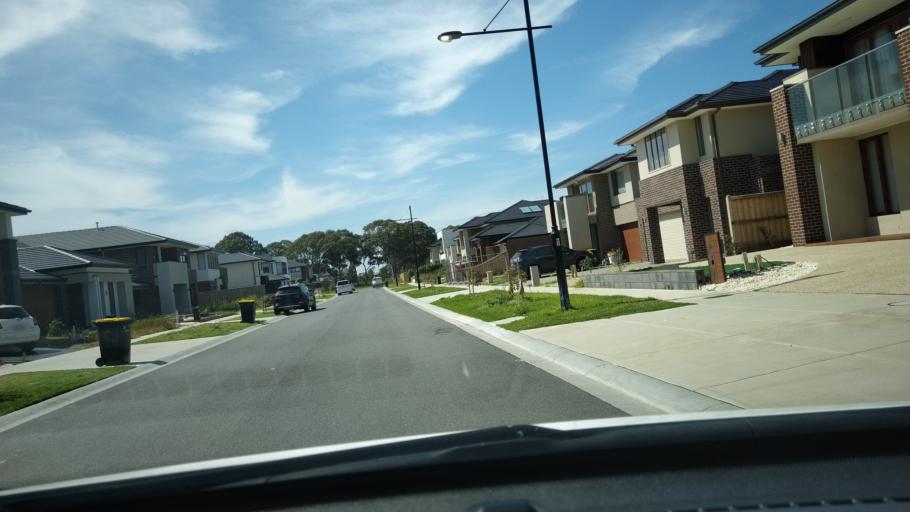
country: AU
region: Victoria
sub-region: Greater Dandenong
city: Keysborough
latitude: -38.0034
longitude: 145.1744
